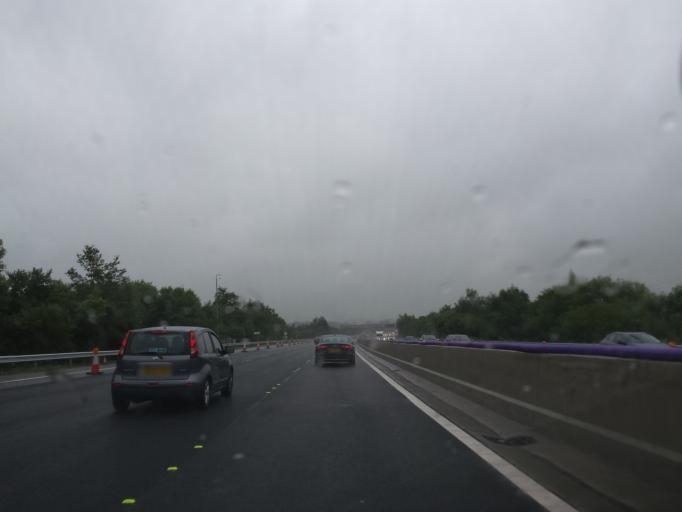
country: GB
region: England
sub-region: Derbyshire
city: Tibshelf
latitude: 53.1864
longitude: -1.3232
